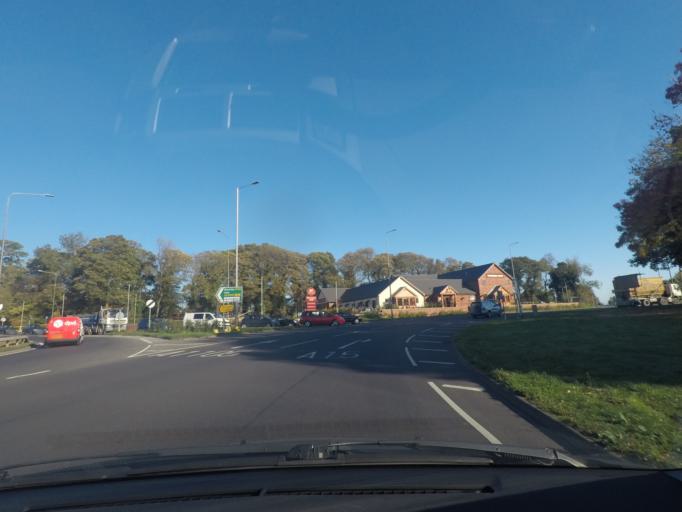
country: GB
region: England
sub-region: East Riding of Yorkshire
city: Hessle
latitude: 53.7252
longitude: -0.4581
